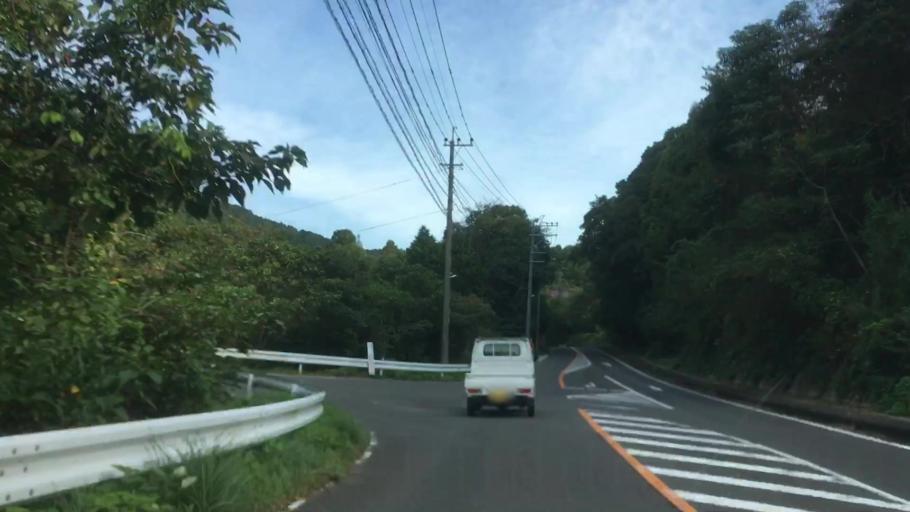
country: JP
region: Nagasaki
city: Sasebo
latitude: 33.0264
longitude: 129.6534
